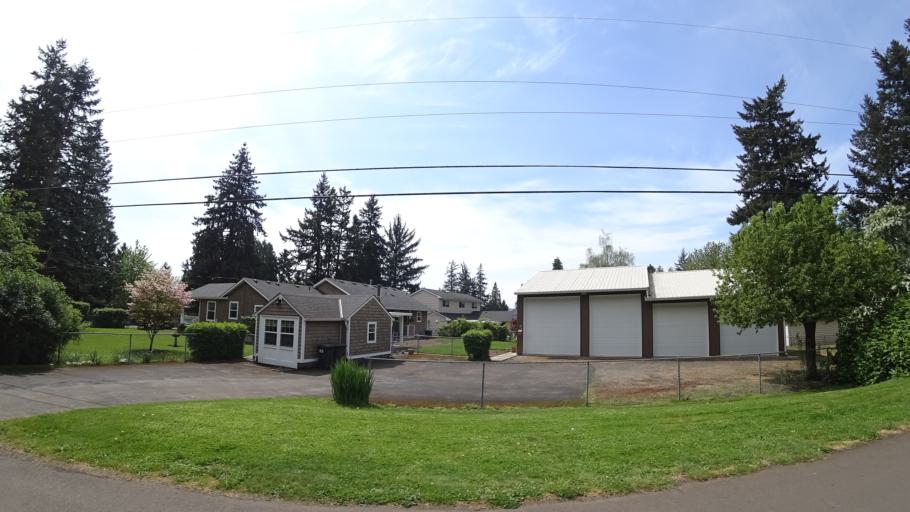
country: US
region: Oregon
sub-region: Clackamas County
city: Milwaukie
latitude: 45.4599
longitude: -122.6027
